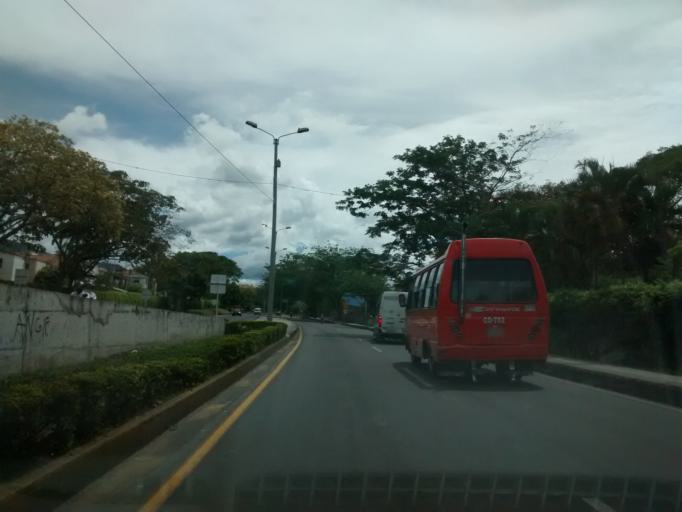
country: CO
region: Tolima
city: Ibague
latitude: 4.4039
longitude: -75.1548
